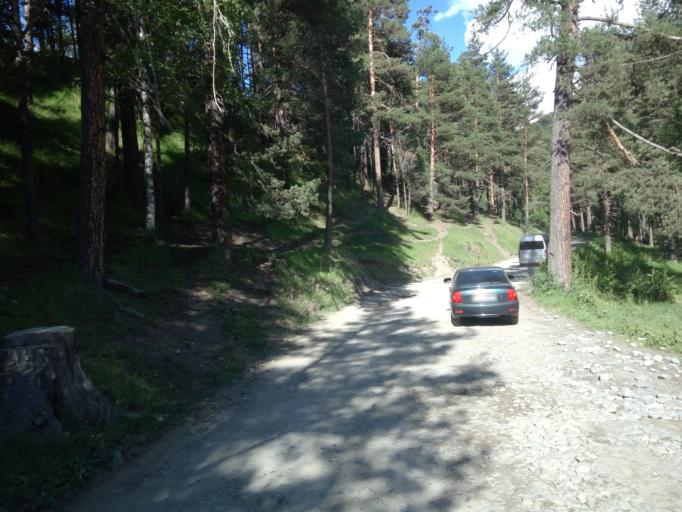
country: RU
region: Karachayevo-Cherkesiya
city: Nizhniy Arkhyz
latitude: 43.5289
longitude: 41.2350
